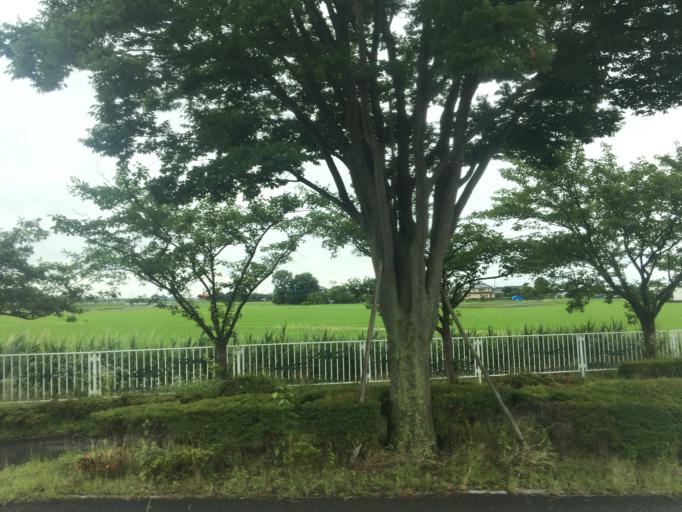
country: JP
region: Saitama
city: Kawagoe
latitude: 35.9322
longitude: 139.5093
